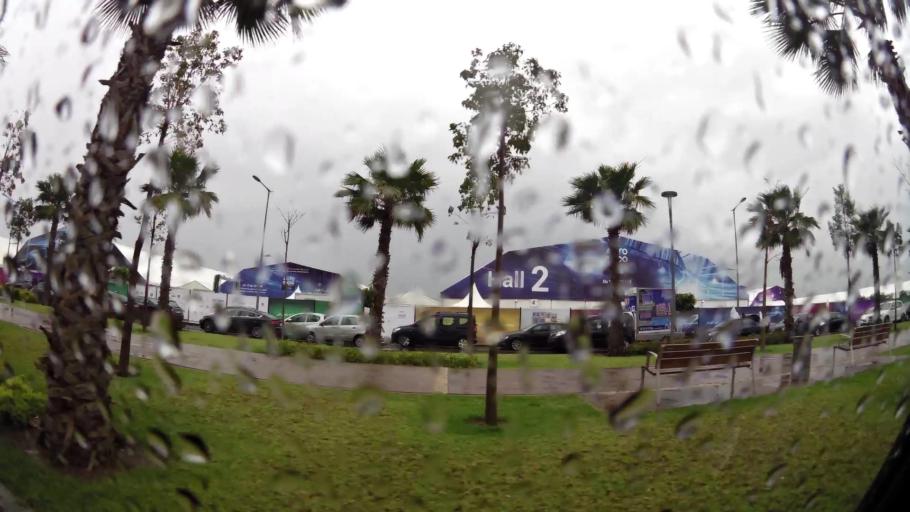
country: MA
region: Grand Casablanca
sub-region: Casablanca
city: Casablanca
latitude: 33.5502
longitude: -7.6665
